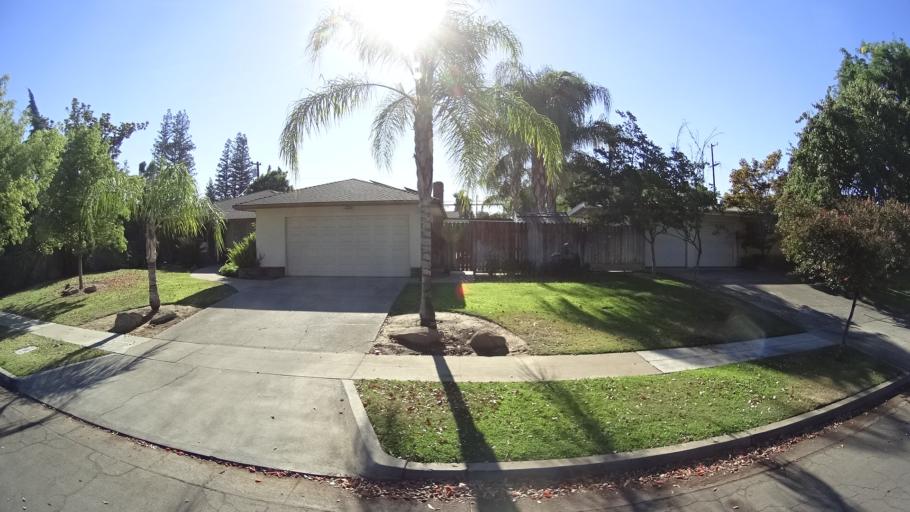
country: US
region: California
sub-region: Fresno County
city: Fresno
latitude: 36.8023
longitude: -119.8276
